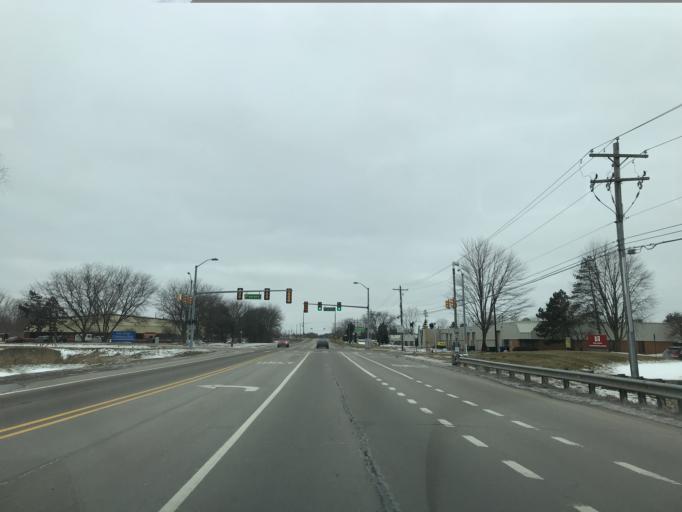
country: US
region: Michigan
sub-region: Washtenaw County
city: Ann Arbor
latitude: 42.2297
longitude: -83.7247
